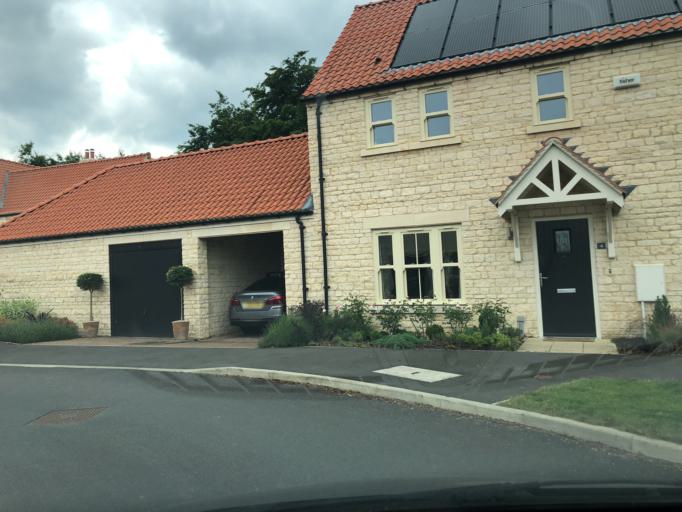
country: GB
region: England
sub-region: North Yorkshire
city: Helmsley
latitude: 54.2482
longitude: -1.0542
